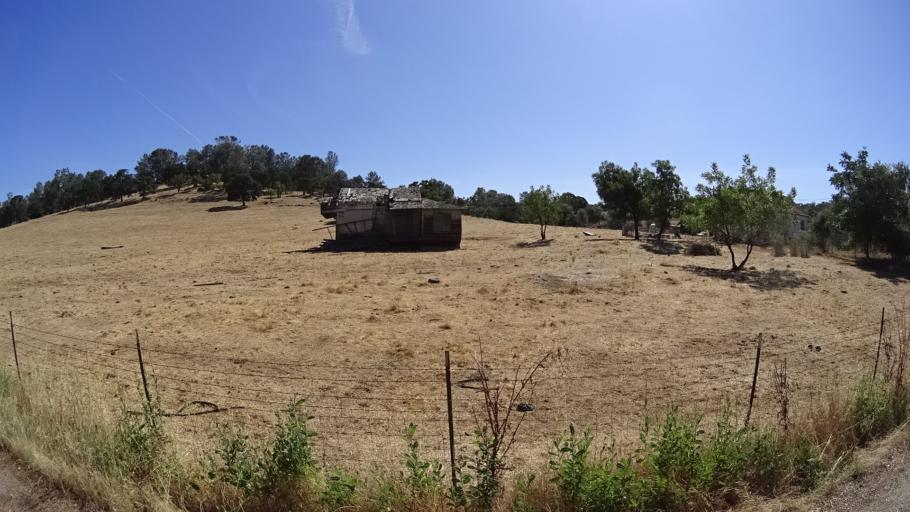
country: US
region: California
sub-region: Calaveras County
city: Valley Springs
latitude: 38.2286
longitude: -120.8544
